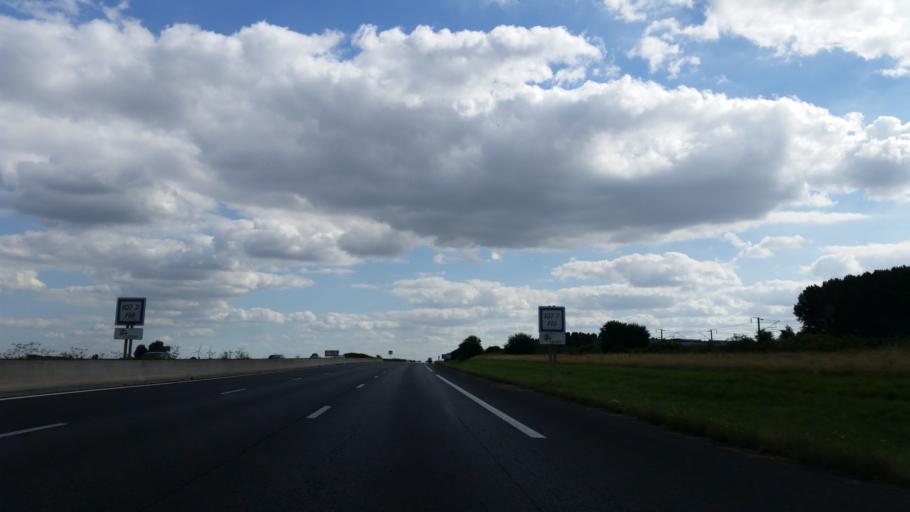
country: FR
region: Nord-Pas-de-Calais
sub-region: Departement du Pas-de-Calais
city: Bapaume
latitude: 50.0945
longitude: 2.8714
